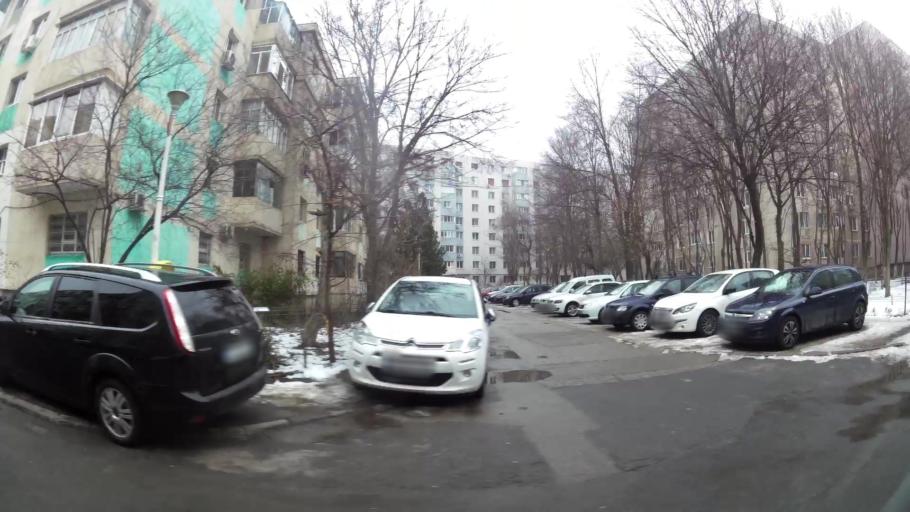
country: RO
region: Ilfov
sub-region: Comuna Chiajna
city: Rosu
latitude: 44.4537
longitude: 26.0433
